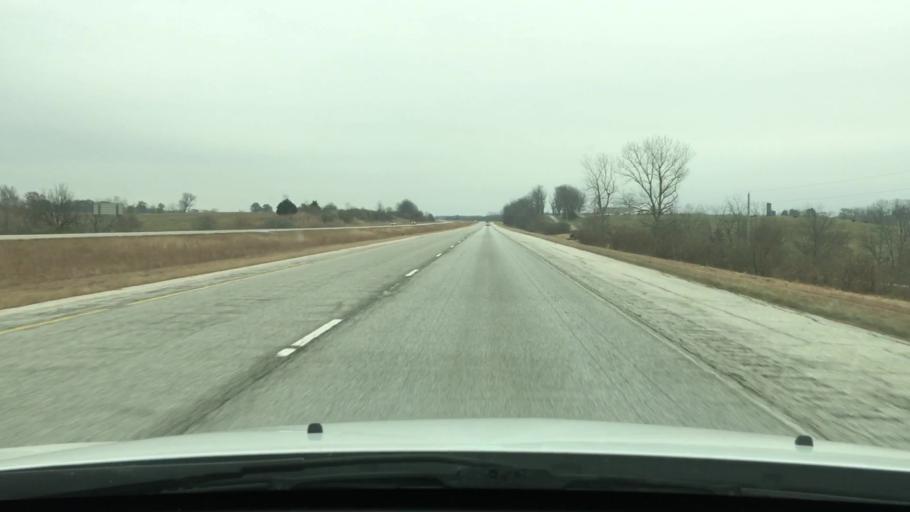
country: US
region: Illinois
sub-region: Morgan County
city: South Jacksonville
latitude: 39.6803
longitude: -90.2796
